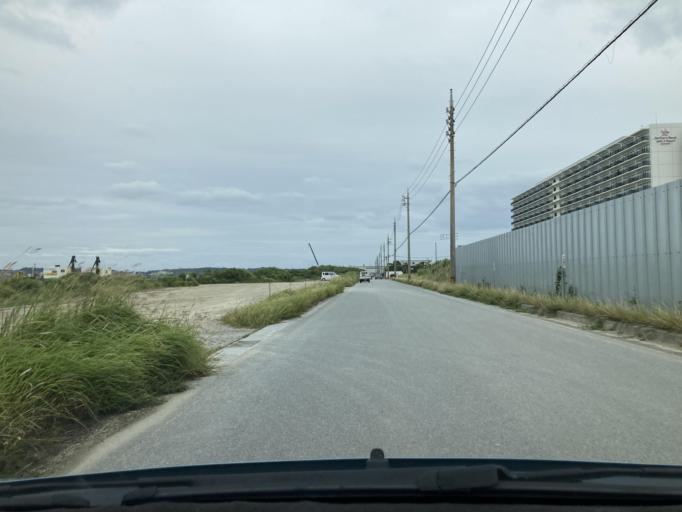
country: JP
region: Okinawa
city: Itoman
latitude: 26.1342
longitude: 127.6532
